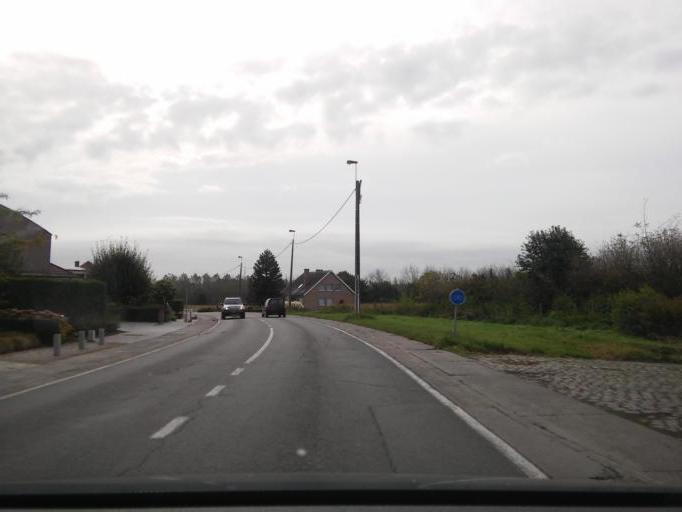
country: BE
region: Flanders
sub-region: Provincie Vlaams-Brabant
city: Lennik
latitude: 50.8042
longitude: 4.1612
